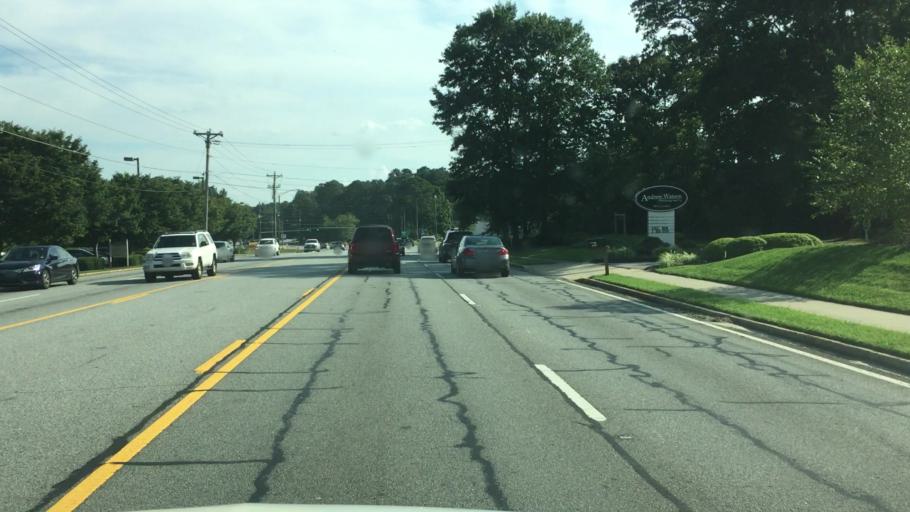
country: US
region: Georgia
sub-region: Gwinnett County
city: Snellville
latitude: 33.8557
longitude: -84.0214
